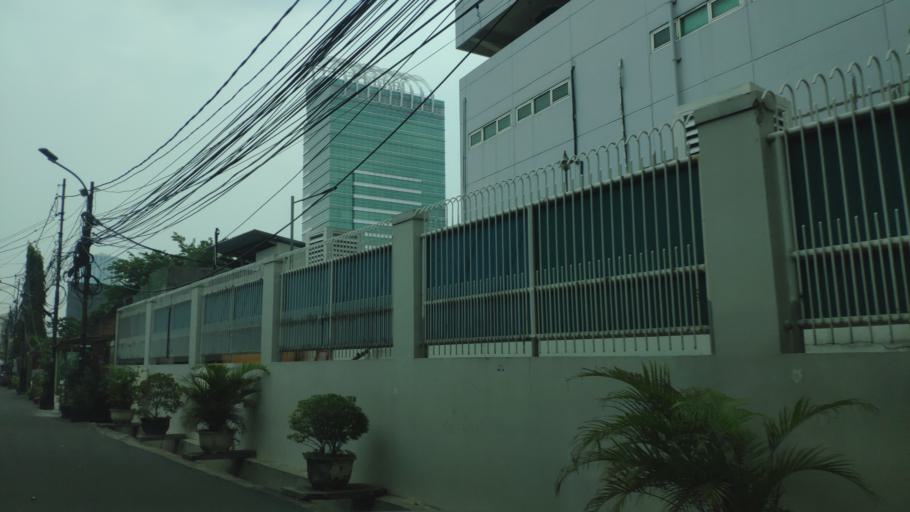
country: ID
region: Jakarta Raya
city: Jakarta
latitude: -6.1907
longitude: 106.7987
